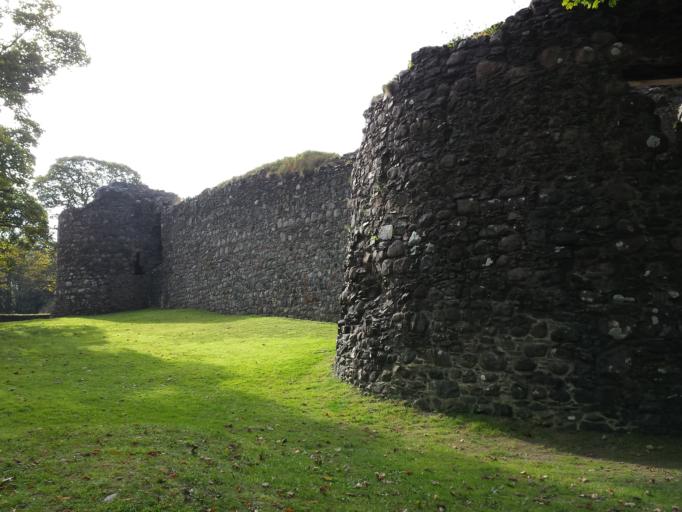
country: GB
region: Scotland
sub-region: Highland
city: Fort William
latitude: 56.8326
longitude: -5.0823
